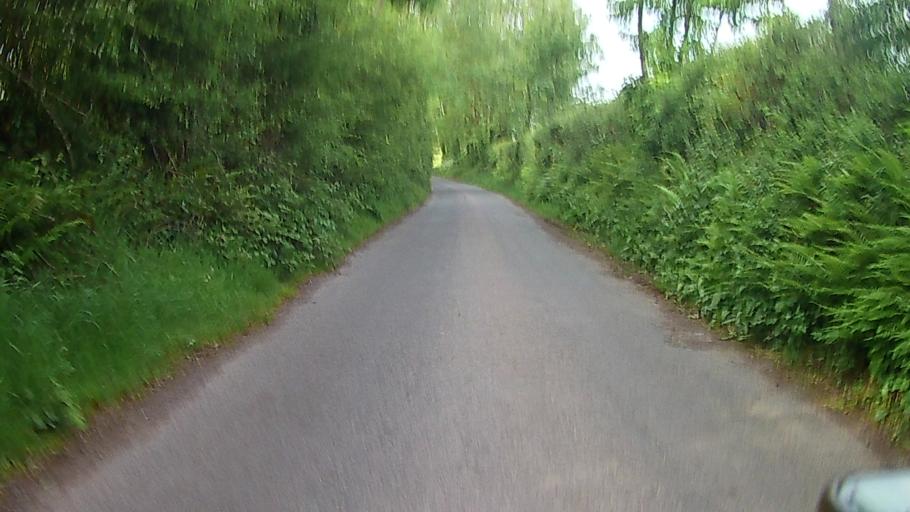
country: IE
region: Munster
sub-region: County Cork
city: Watergrasshill
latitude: 51.9899
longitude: -8.3993
